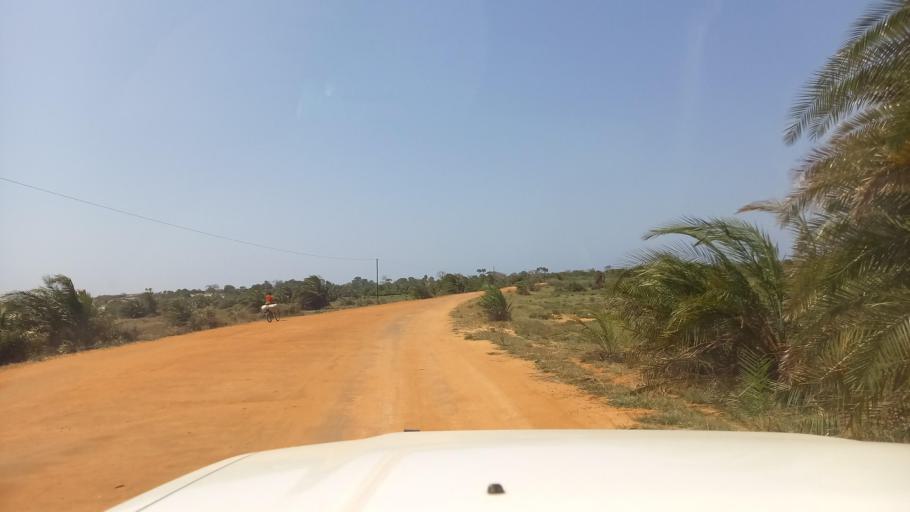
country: MZ
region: Cabo Delgado
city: Pemba
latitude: -13.3925
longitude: 40.5283
